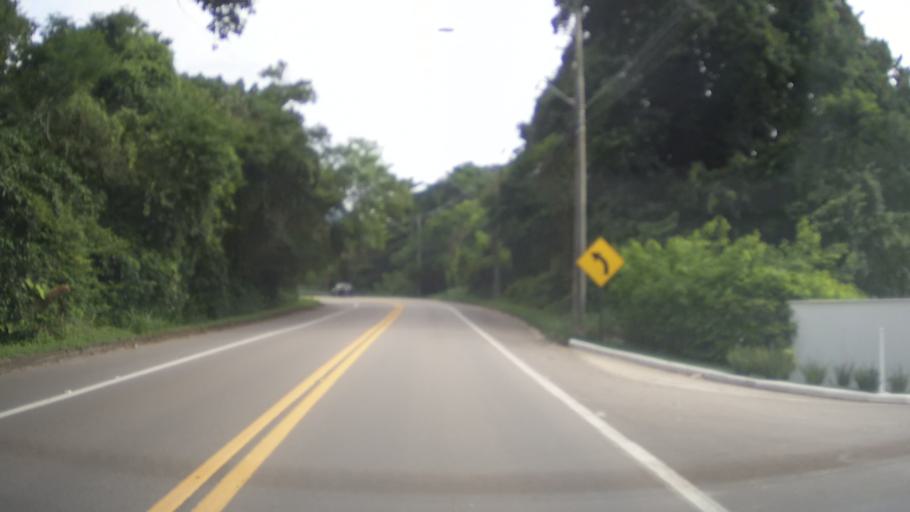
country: BR
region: Sao Paulo
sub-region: Sao Sebastiao
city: Sao Sebastiao
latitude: -23.8221
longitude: -45.4530
